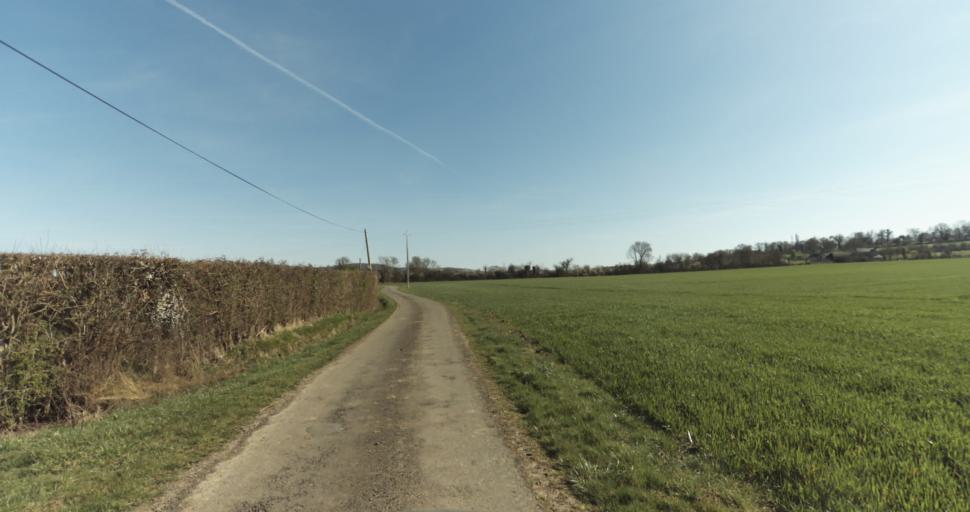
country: FR
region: Lower Normandy
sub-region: Departement du Calvados
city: Saint-Pierre-sur-Dives
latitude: 49.0346
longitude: 0.0070
